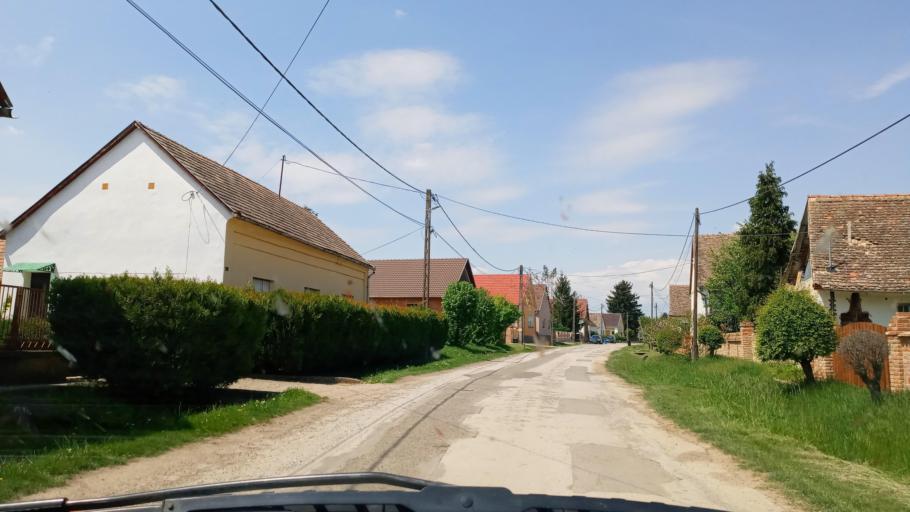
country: HU
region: Baranya
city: Villany
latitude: 45.8712
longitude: 18.5127
